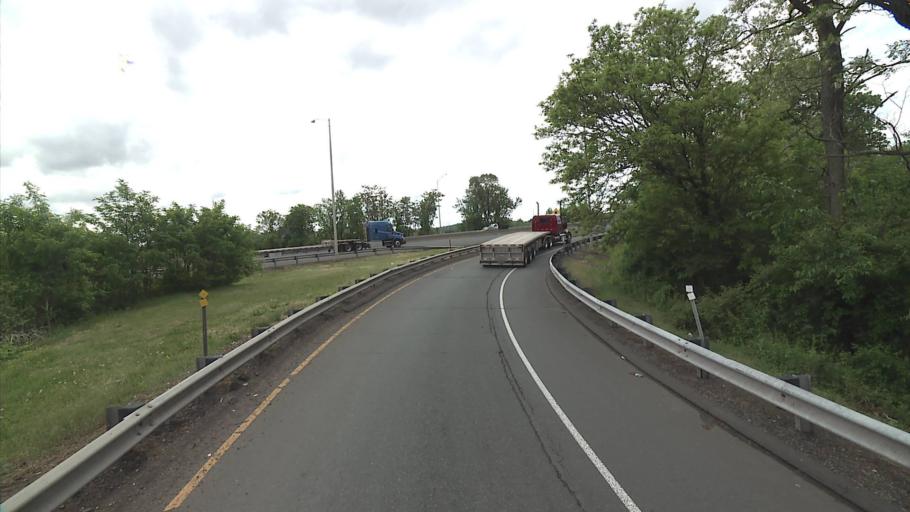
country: US
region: Connecticut
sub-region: New Haven County
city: New Haven
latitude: 41.3258
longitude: -72.8822
